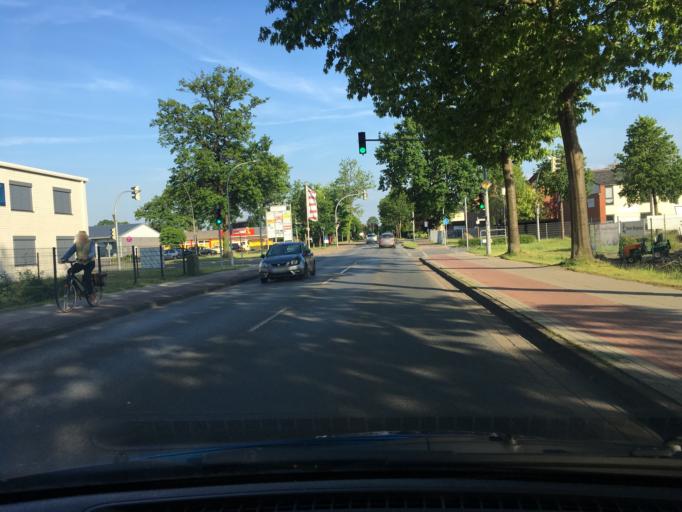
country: DE
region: Lower Saxony
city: Tostedt
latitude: 53.2683
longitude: 9.7269
